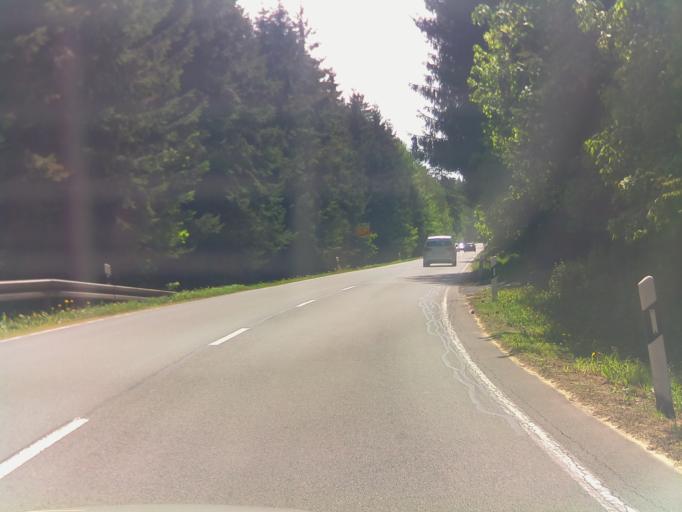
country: DE
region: Saxony-Anhalt
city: Hasselfelde
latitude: 51.6761
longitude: 10.8373
